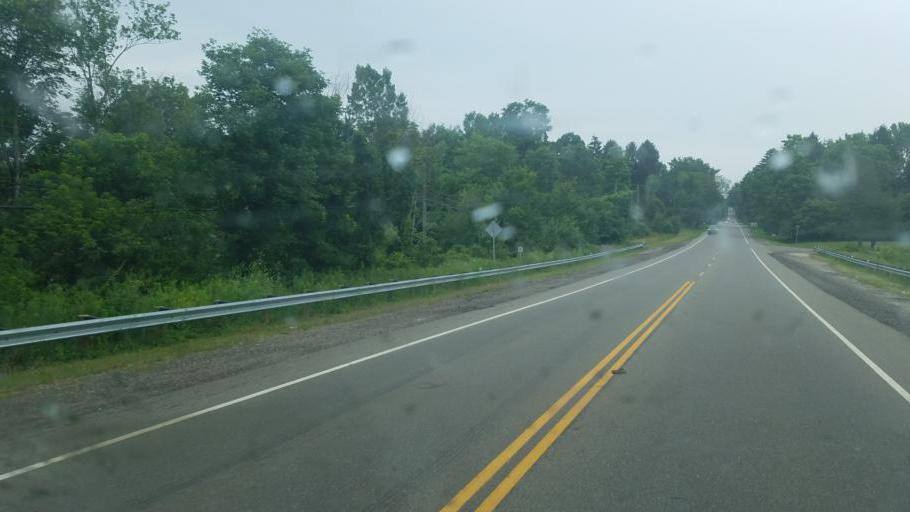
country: US
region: Ohio
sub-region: Summit County
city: Portage Lakes
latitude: 40.9815
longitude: -81.5612
